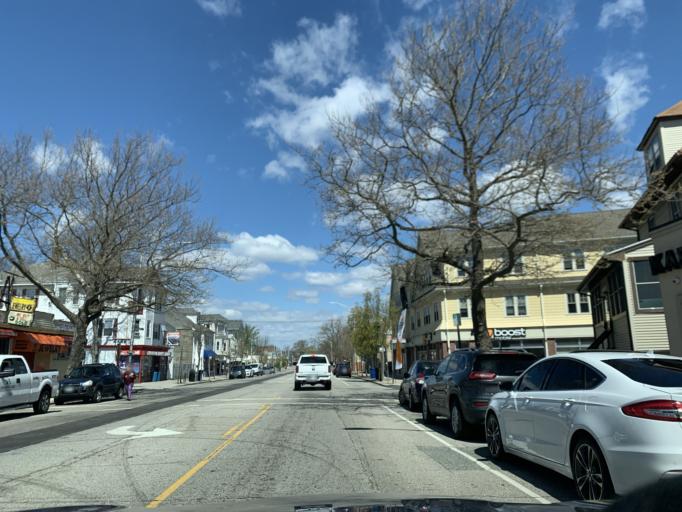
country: US
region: Rhode Island
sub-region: Providence County
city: Cranston
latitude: 41.7890
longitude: -71.4041
